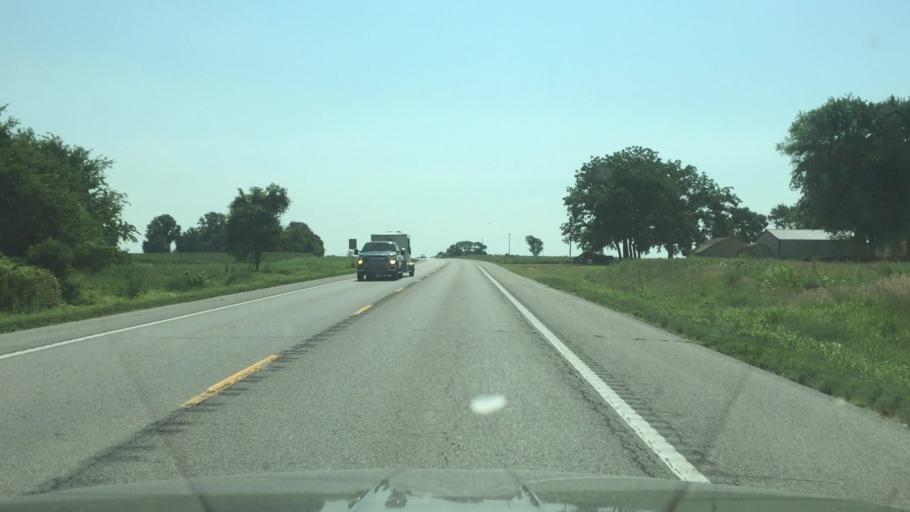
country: US
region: Missouri
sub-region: Pettis County
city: Sedalia
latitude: 38.6919
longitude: -93.0659
